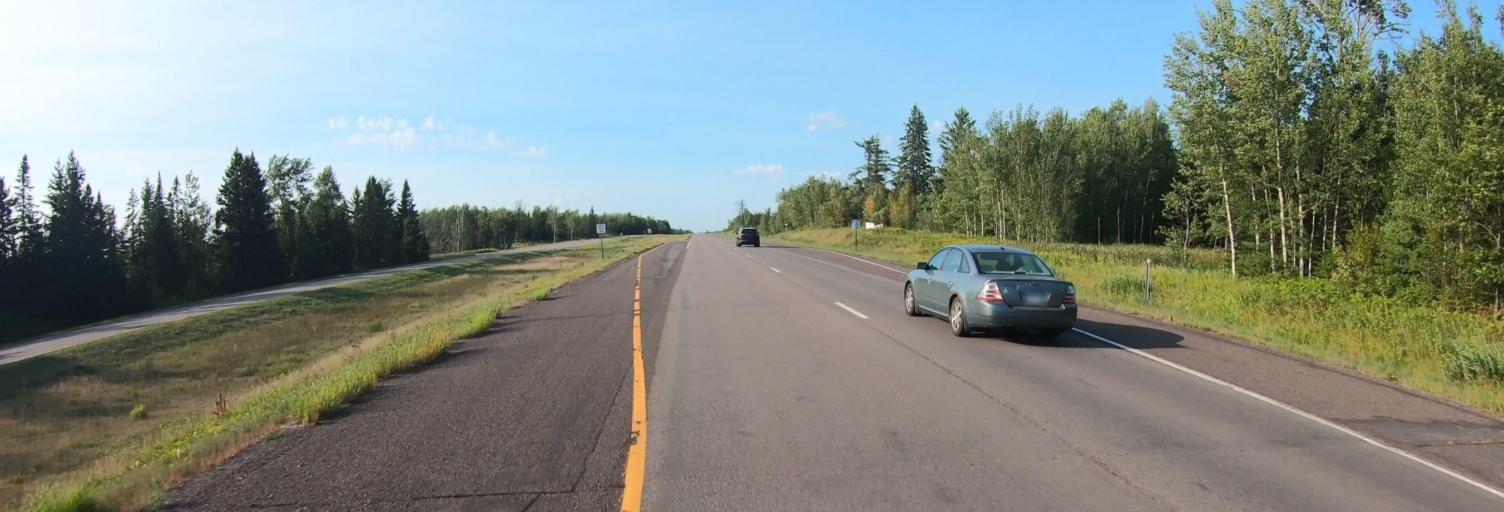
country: US
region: Minnesota
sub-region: Carlton County
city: Cloquet
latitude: 47.0076
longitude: -92.4711
